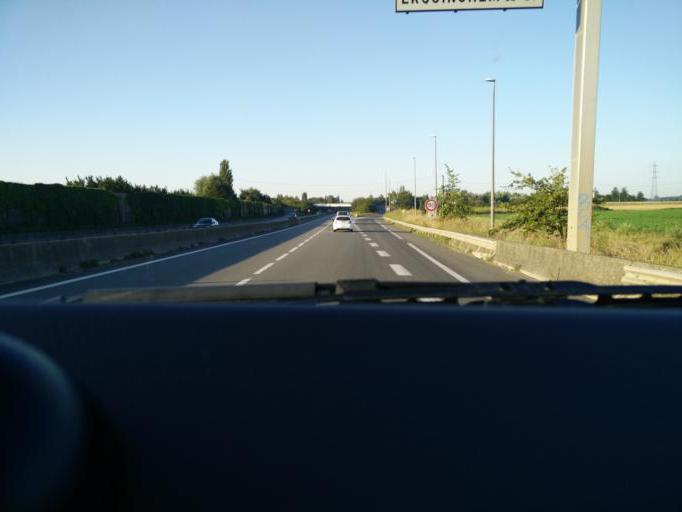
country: FR
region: Nord-Pas-de-Calais
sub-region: Departement du Nord
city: Hallennes-lez-Haubourdin
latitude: 50.6147
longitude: 2.9543
